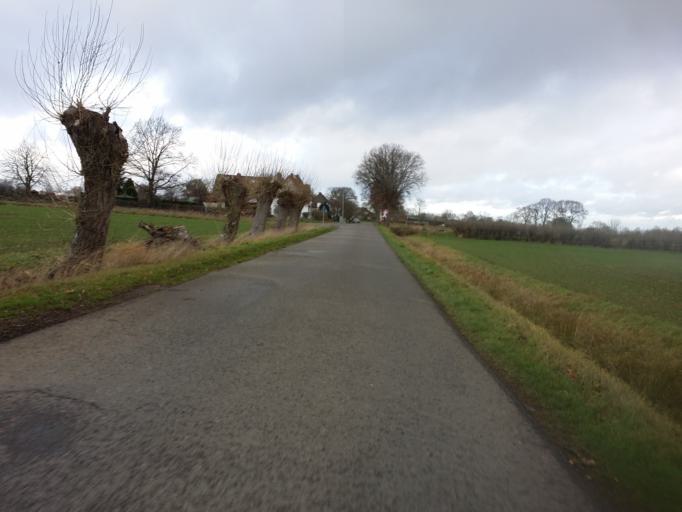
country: DE
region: Lower Saxony
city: Thedinghausen
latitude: 52.9683
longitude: 8.9902
